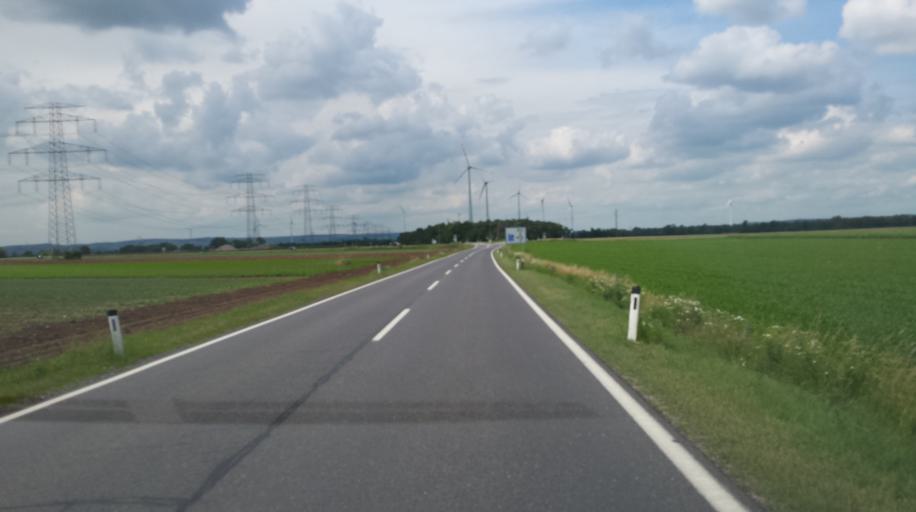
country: AT
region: Lower Austria
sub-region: Politischer Bezirk Mistelbach
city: Pillichsdorf
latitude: 48.3199
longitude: 16.5310
